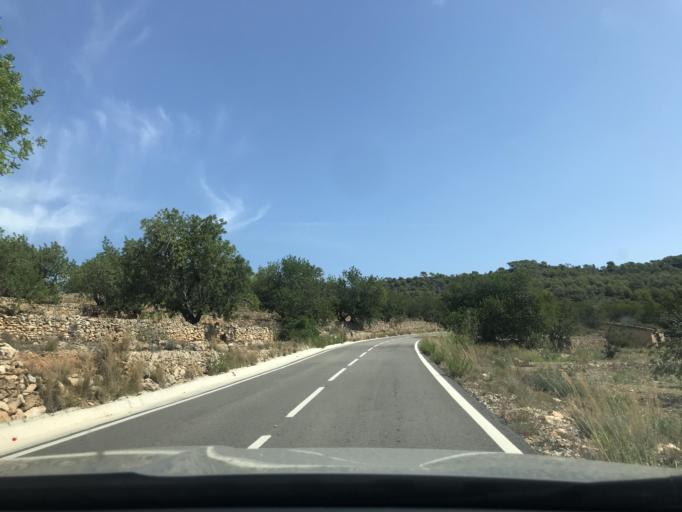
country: ES
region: Catalonia
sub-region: Provincia de Tarragona
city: Salomo
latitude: 41.2031
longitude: 1.3869
